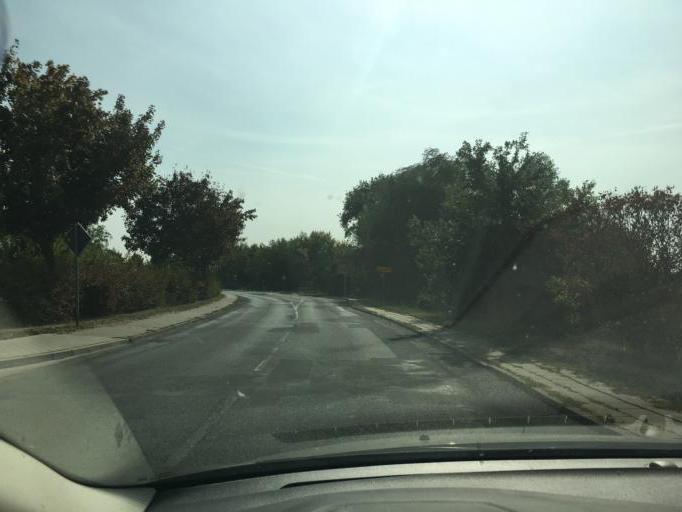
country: DE
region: Saxony-Anhalt
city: Barby
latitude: 51.9697
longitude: 11.8759
